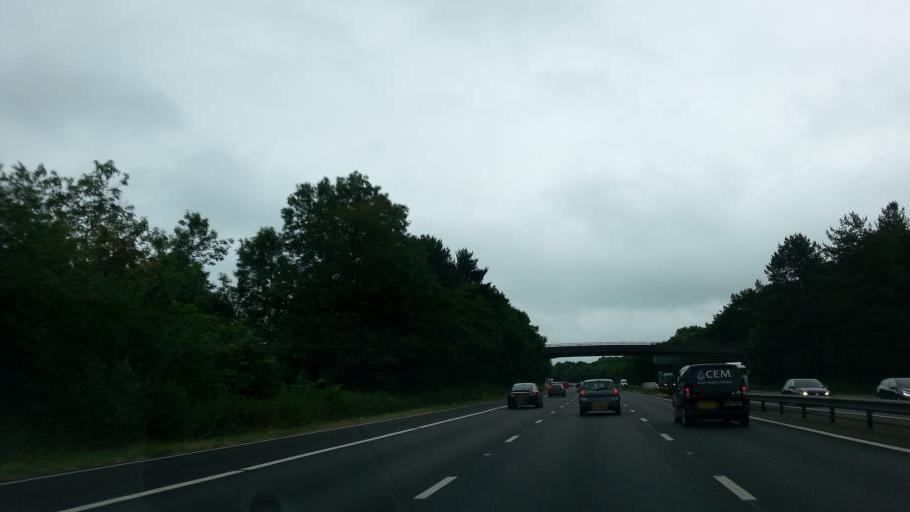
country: GB
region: England
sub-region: Leicestershire
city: Lutterworth
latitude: 52.4929
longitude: -1.1911
